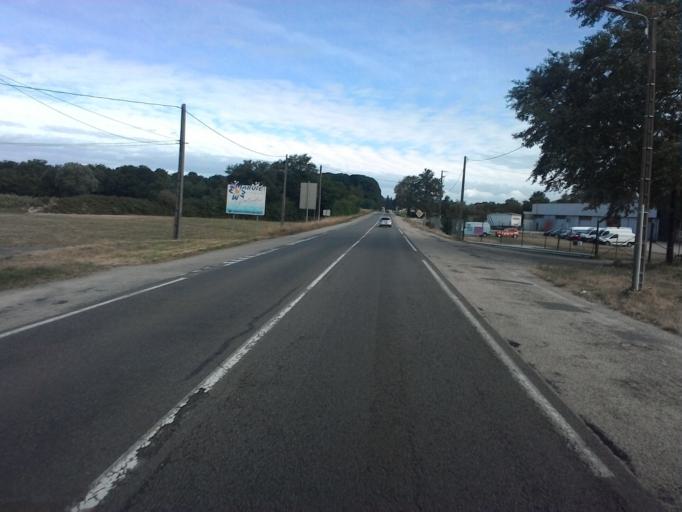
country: FR
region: Rhone-Alpes
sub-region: Departement de l'Ain
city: Montagnat
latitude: 46.1569
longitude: 5.2733
